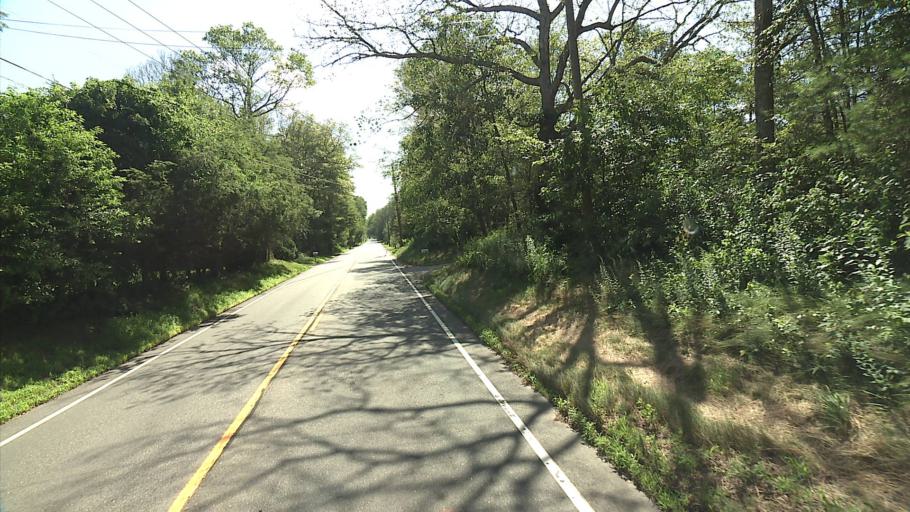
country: US
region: Connecticut
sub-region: New London County
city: Baltic
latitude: 41.7099
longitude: -72.0334
